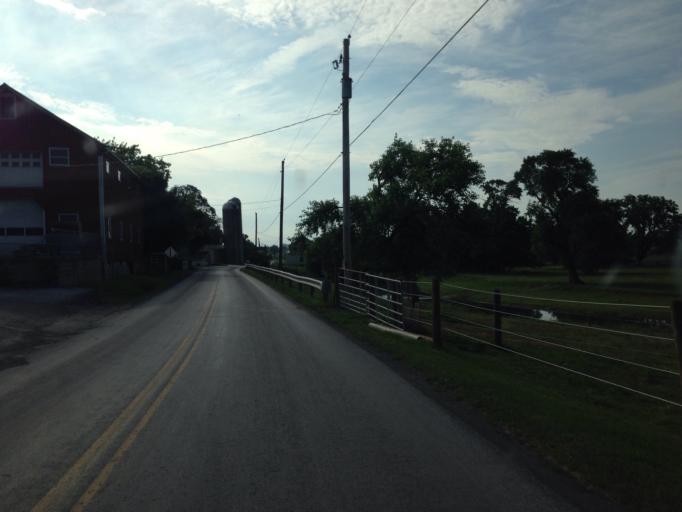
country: US
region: Pennsylvania
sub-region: Lancaster County
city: Strasburg
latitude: 40.0524
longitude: -76.1896
